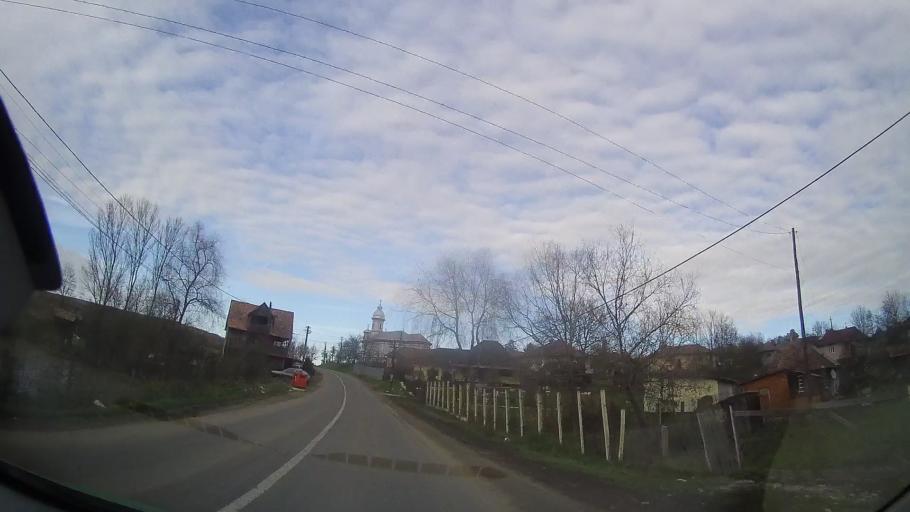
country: RO
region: Cluj
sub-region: Comuna Geaca
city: Geaca
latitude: 46.8531
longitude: 24.0914
